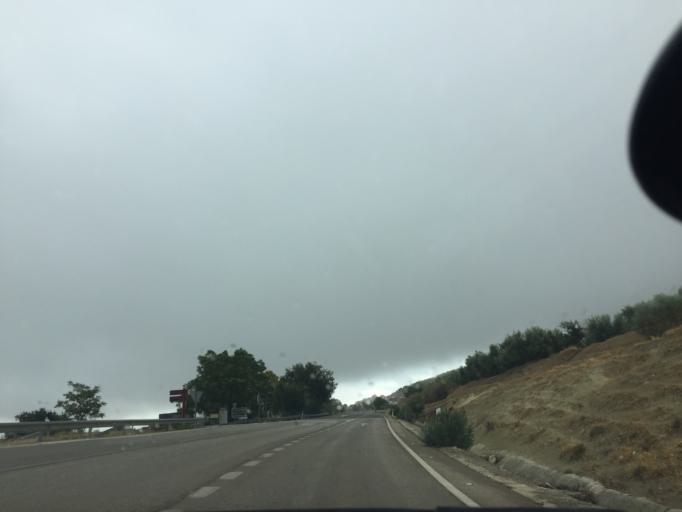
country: ES
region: Andalusia
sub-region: Provincia de Jaen
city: Jimena
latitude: 37.8457
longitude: -3.4875
